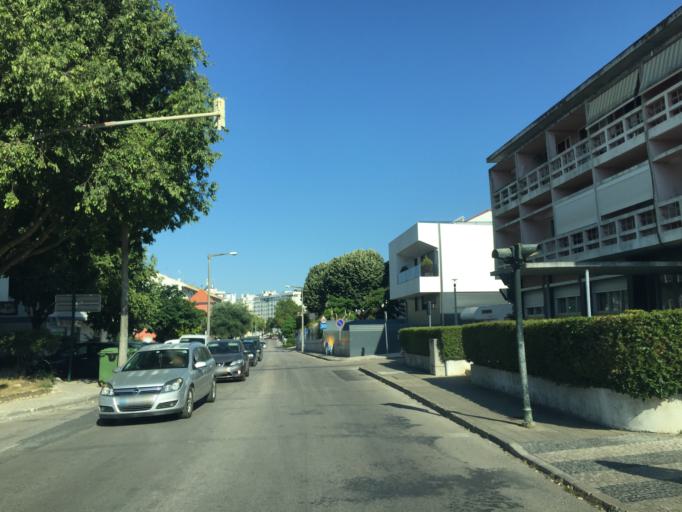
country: PT
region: Santarem
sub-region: Tomar
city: Tomar
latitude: 39.6042
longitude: -8.4026
